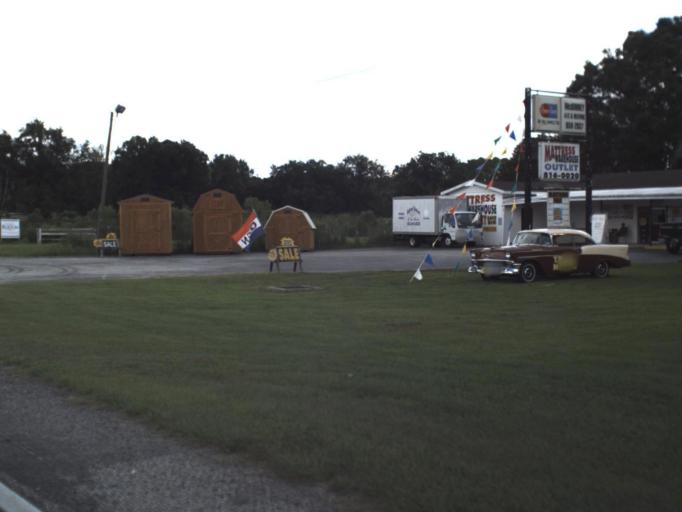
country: US
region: Florida
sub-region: Polk County
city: Gibsonia
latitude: 28.1451
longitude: -81.9736
